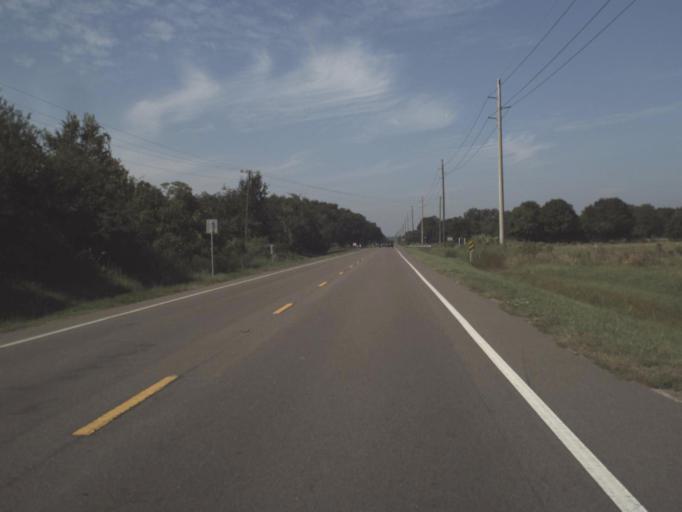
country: US
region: Florida
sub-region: Hardee County
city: Wauchula
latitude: 27.5515
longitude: -81.7414
